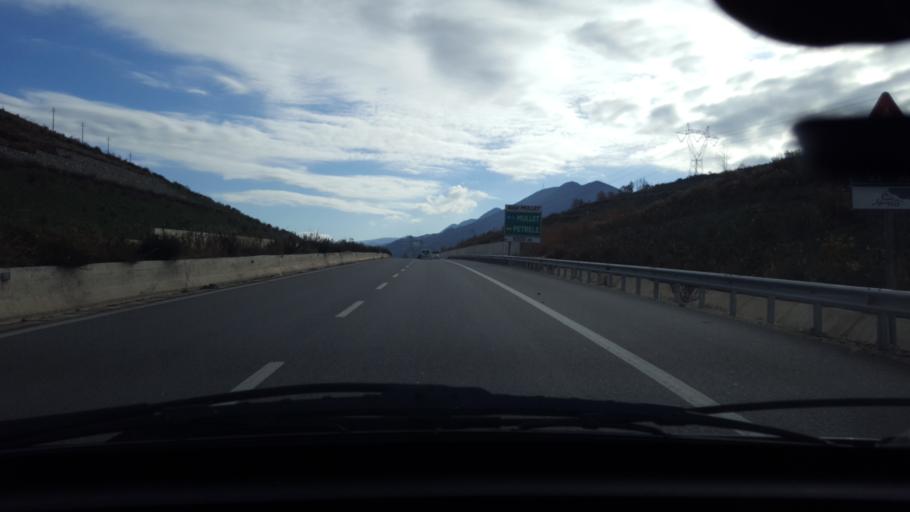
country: AL
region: Tirane
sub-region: Rrethi i Tiranes
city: Petrele
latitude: 41.2705
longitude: 19.8611
